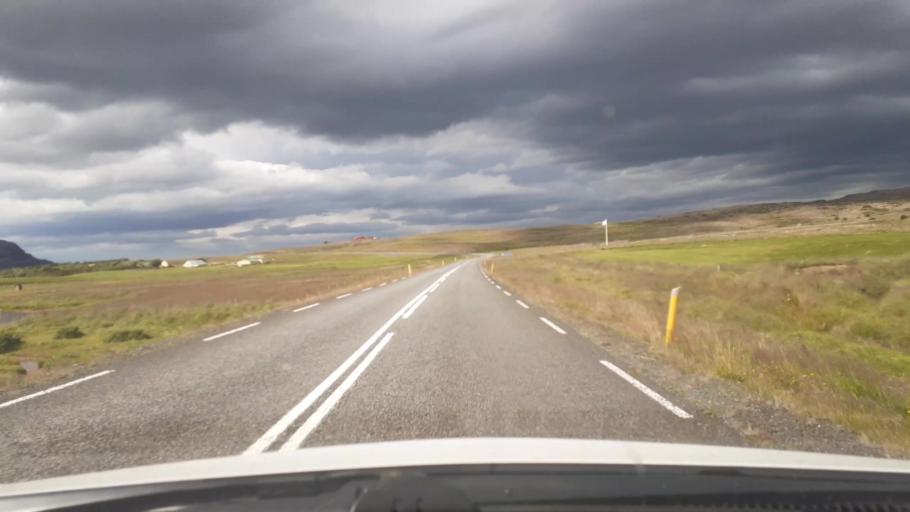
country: IS
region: West
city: Borgarnes
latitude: 64.5451
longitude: -21.6403
